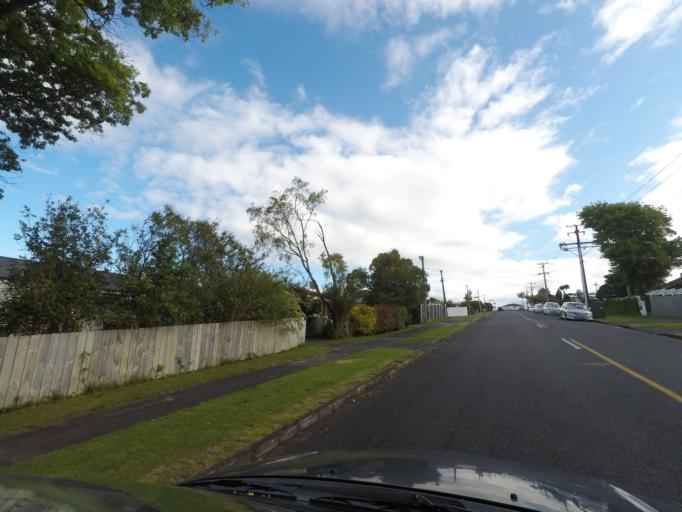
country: NZ
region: Auckland
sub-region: Auckland
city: Rosebank
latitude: -36.8833
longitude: 174.6518
